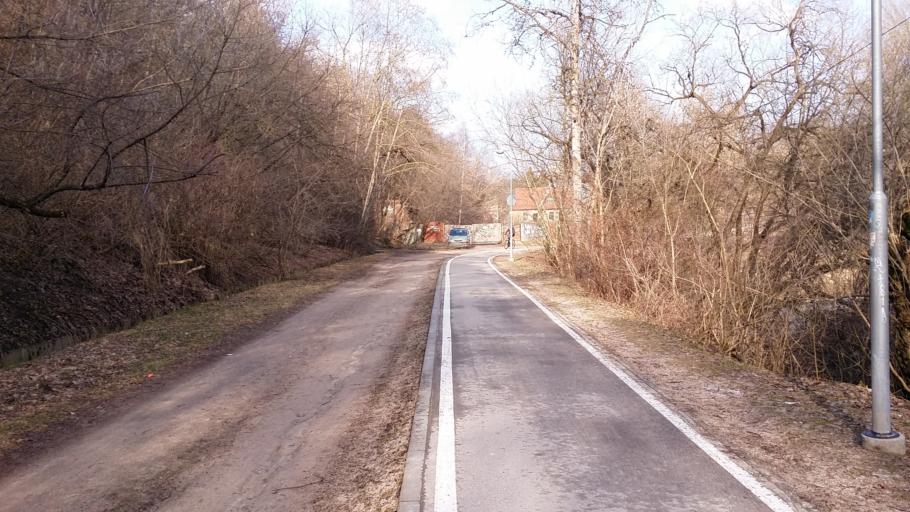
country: LT
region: Vilnius County
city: Rasos
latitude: 54.7093
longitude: 25.3075
